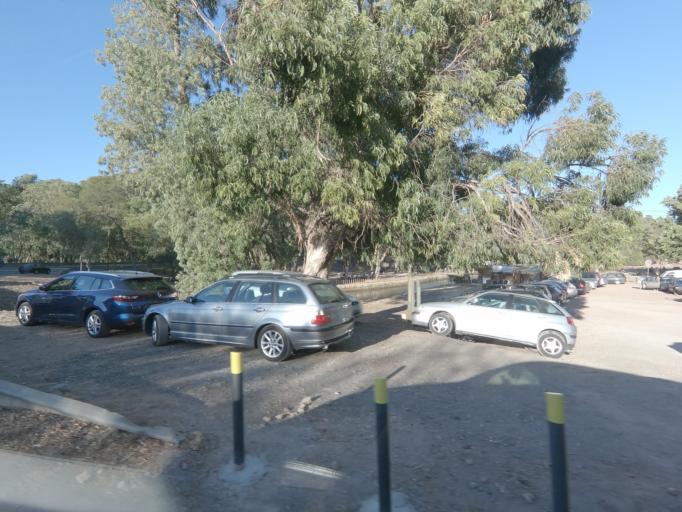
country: PT
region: Setubal
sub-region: Setubal
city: Setubal
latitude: 38.5081
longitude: -8.9291
